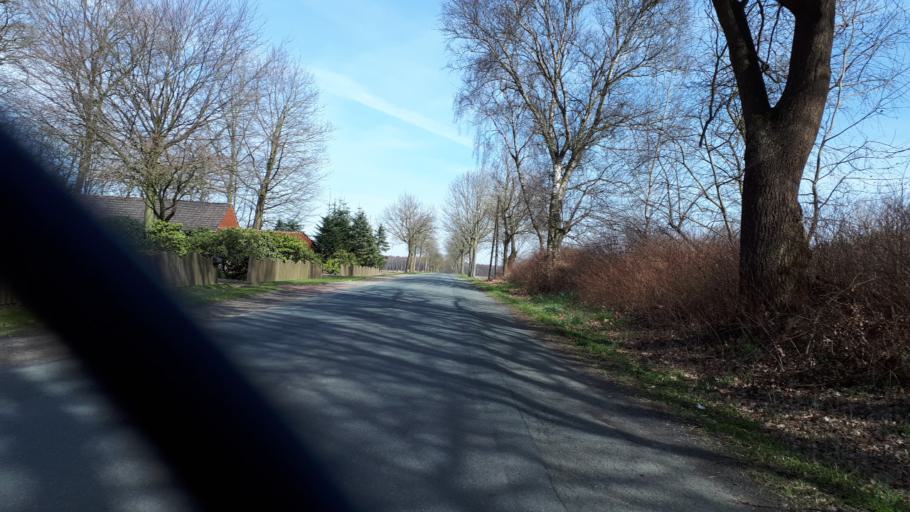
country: DE
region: Lower Saxony
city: Cloppenburg
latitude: 52.8752
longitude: 7.9992
